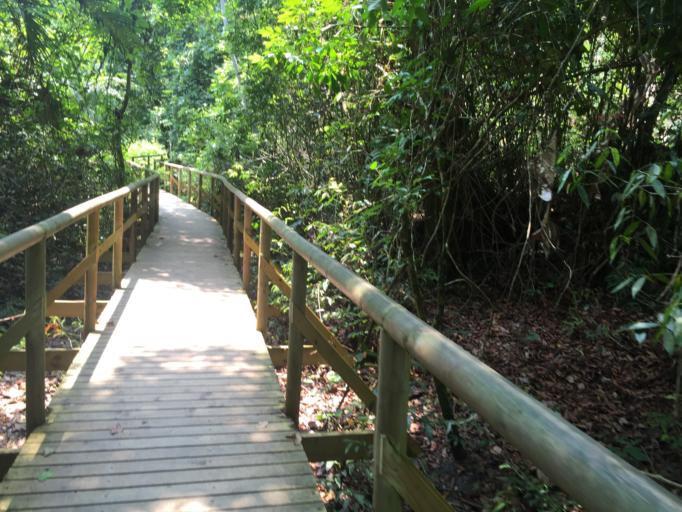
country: CR
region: Puntarenas
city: Quepos
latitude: 9.3849
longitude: -84.1430
